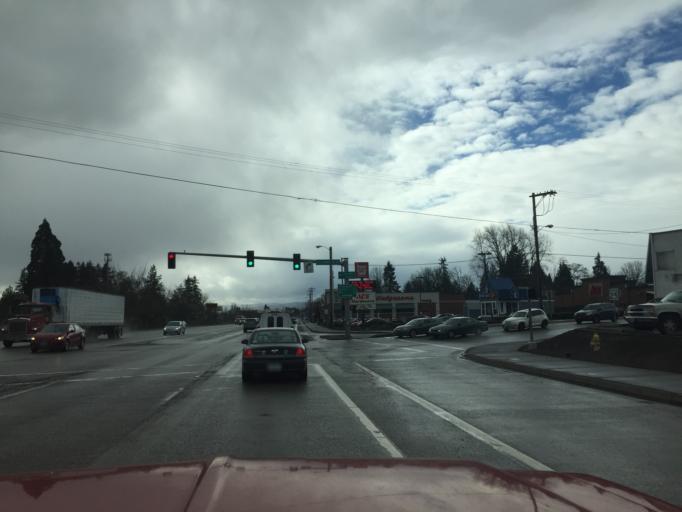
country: US
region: Oregon
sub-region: Columbia County
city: Saint Helens
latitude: 45.8592
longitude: -122.8212
